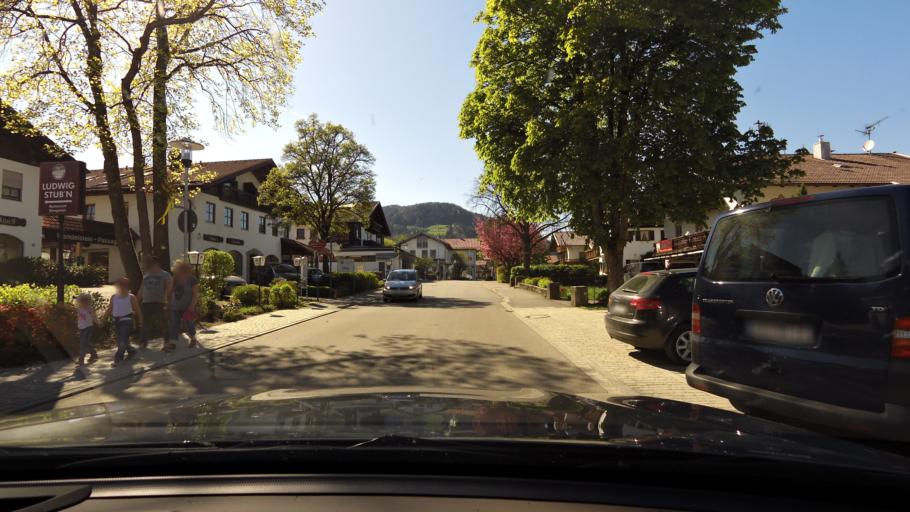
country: DE
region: Bavaria
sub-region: Upper Bavaria
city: Bad Feilnbach
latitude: 47.7733
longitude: 12.0086
